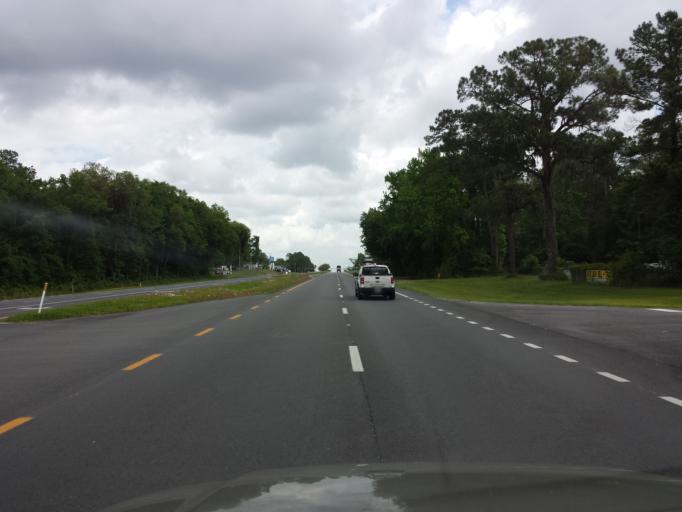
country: US
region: Florida
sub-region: Columbia County
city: Lake City
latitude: 30.1581
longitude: -82.6430
